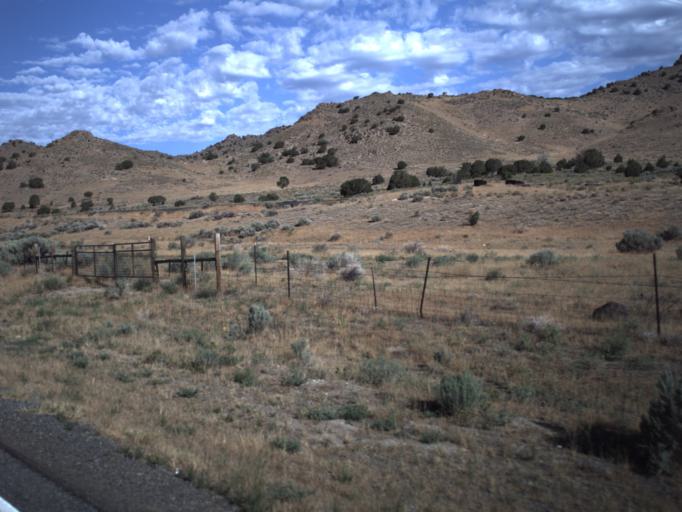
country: US
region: Utah
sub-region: Utah County
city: Genola
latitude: 39.9506
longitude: -112.0120
